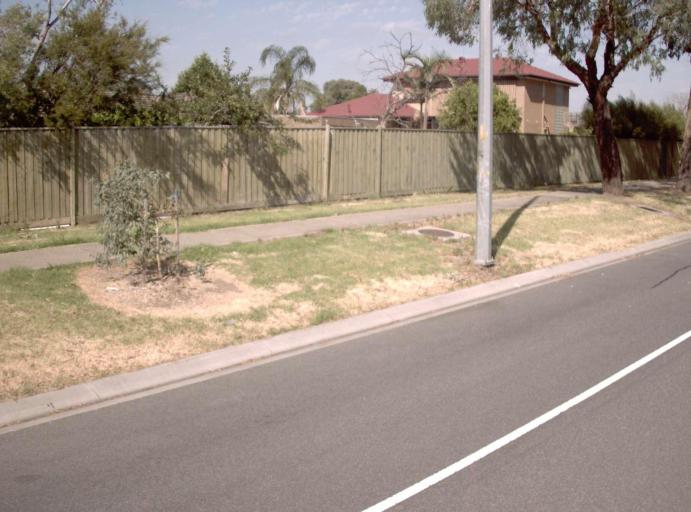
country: AU
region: Victoria
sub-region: Knox
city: Knoxfield
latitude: -37.9126
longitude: 145.2528
